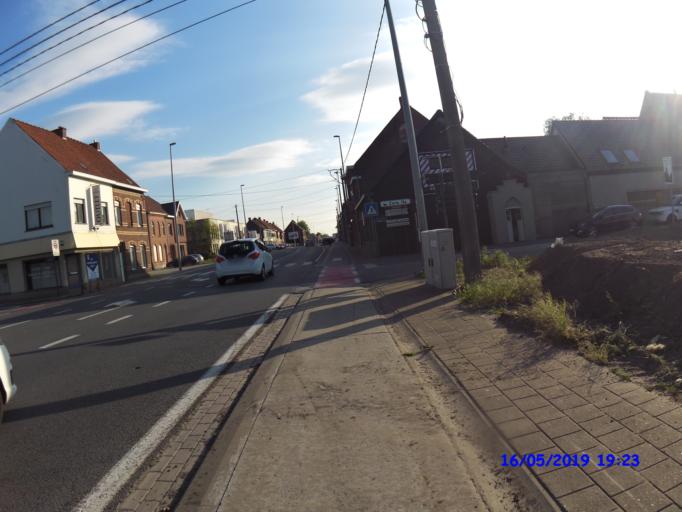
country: BE
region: Flanders
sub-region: Provincie West-Vlaanderen
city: Deerlijk
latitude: 50.8693
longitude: 3.3367
